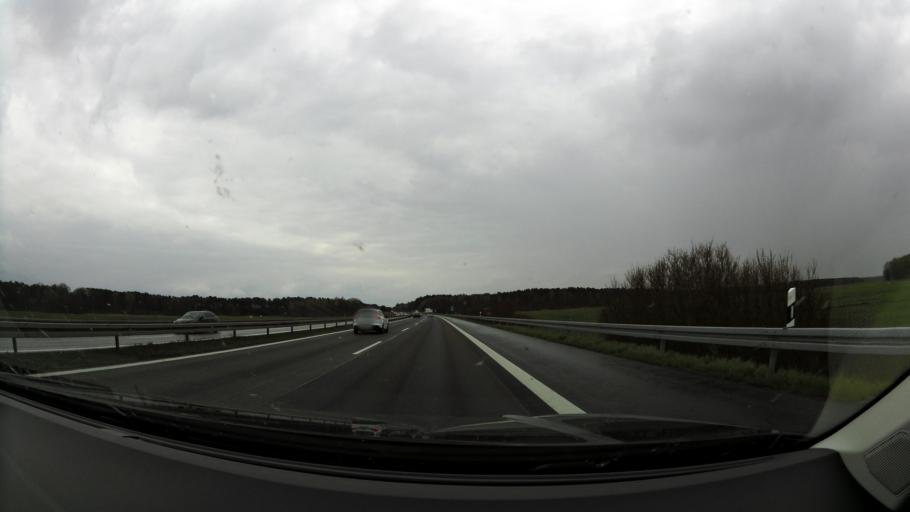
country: DE
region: Brandenburg
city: Wittstock
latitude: 53.0496
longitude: 12.5423
